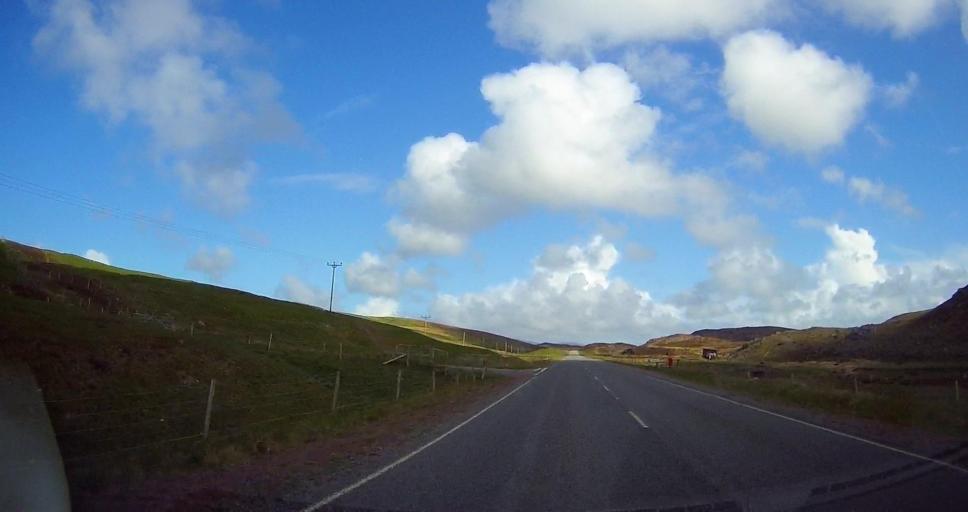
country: GB
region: Scotland
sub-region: Shetland Islands
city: Lerwick
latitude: 60.4259
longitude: -1.3962
